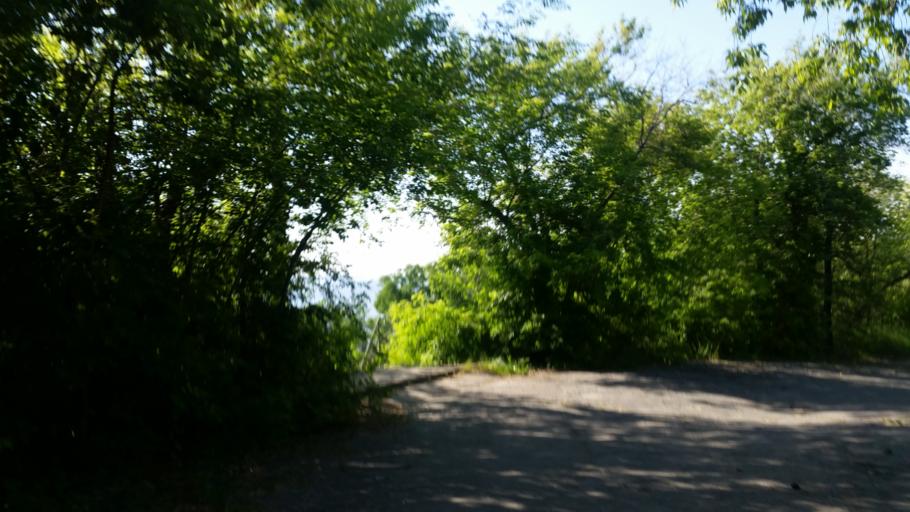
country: RU
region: Ulyanovsk
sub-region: Ulyanovskiy Rayon
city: Ulyanovsk
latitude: 54.3096
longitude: 48.4116
